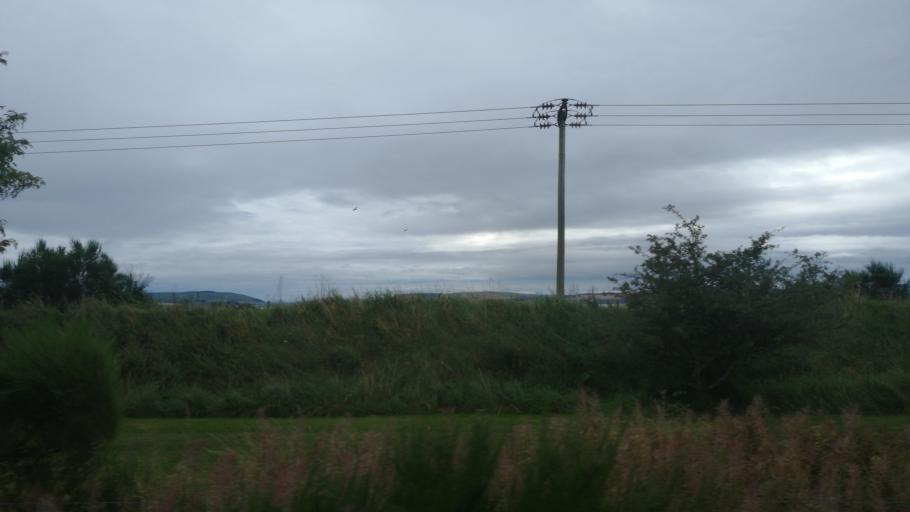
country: GB
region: Scotland
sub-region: Highland
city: Invergordon
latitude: 57.7242
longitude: -4.1104
